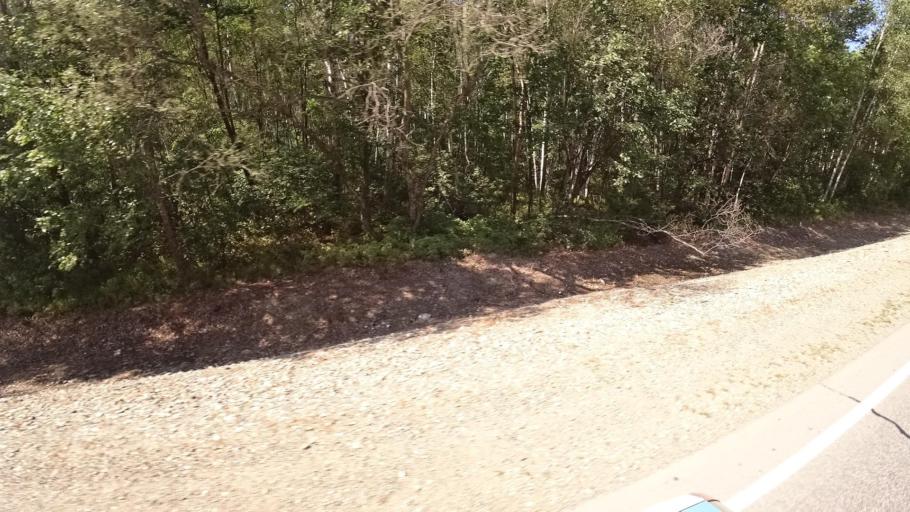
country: RU
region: Khabarovsk Krai
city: Khor
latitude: 47.9817
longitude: 135.0871
